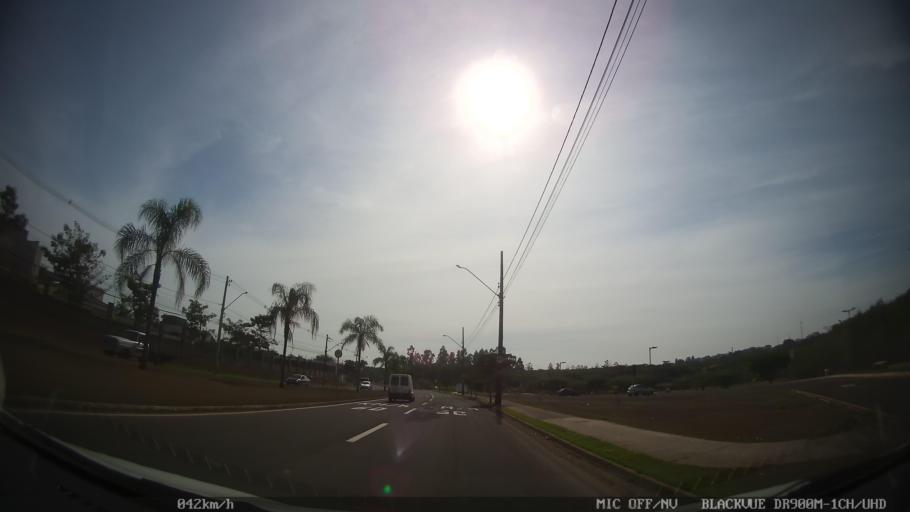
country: BR
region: Sao Paulo
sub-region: Piracicaba
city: Piracicaba
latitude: -22.7036
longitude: -47.6760
